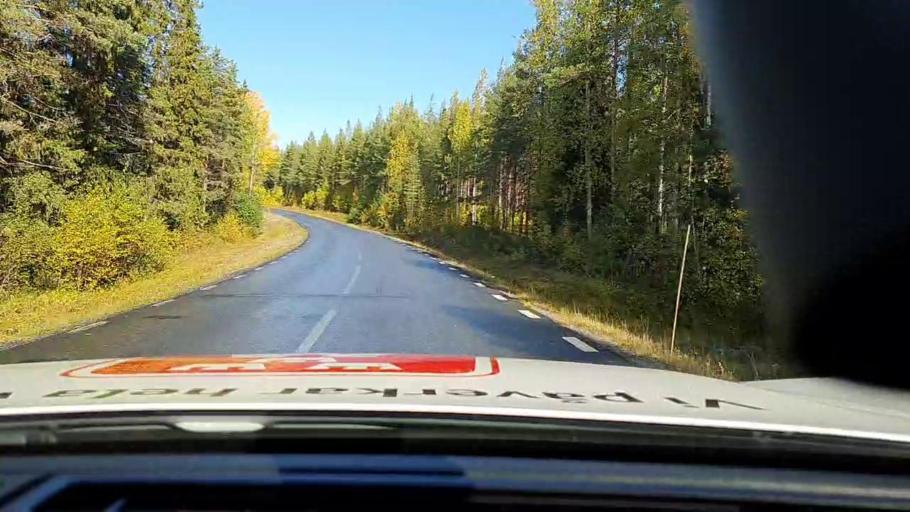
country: SE
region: Vaesterbotten
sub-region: Skelleftea Kommun
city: Langsele
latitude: 64.9620
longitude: 20.0437
